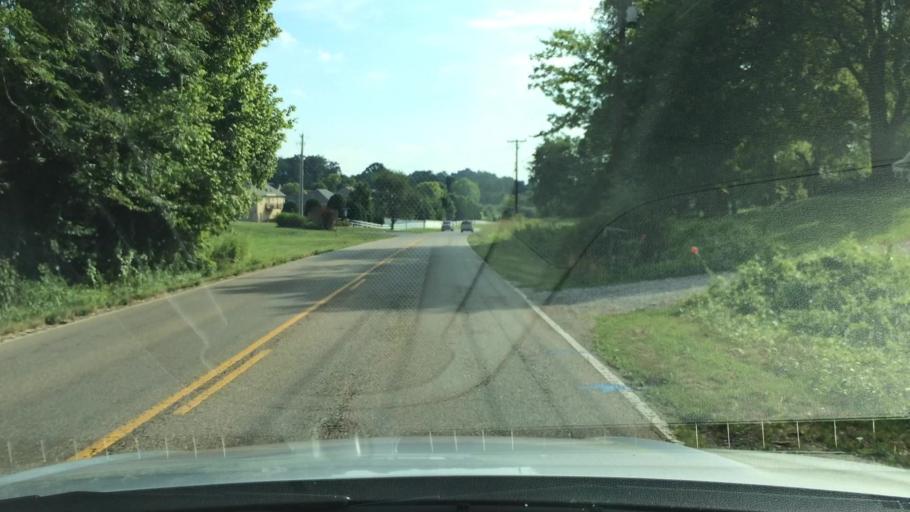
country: US
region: Tennessee
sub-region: Sevier County
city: Seymour
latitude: 35.8979
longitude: -83.7075
